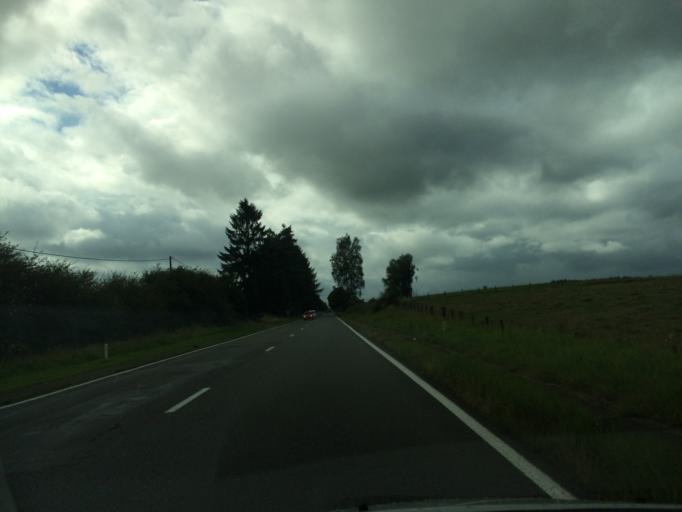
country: BE
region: Wallonia
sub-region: Province du Luxembourg
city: Florenville
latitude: 49.6883
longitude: 5.3507
